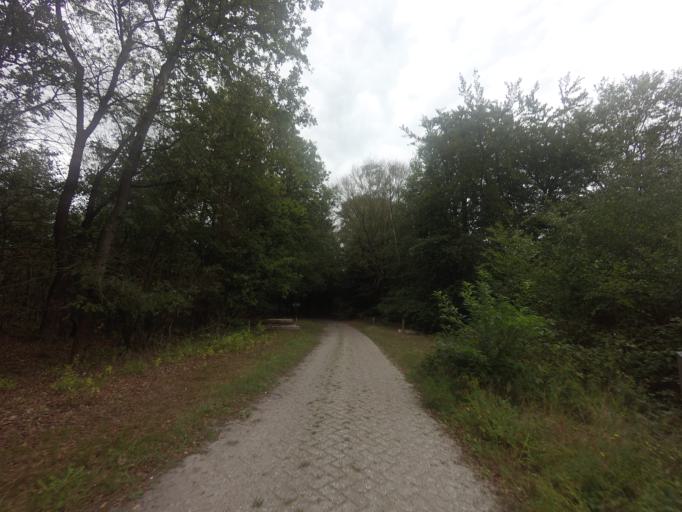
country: NL
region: Drenthe
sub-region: Gemeente Westerveld
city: Dwingeloo
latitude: 52.9233
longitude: 6.3375
